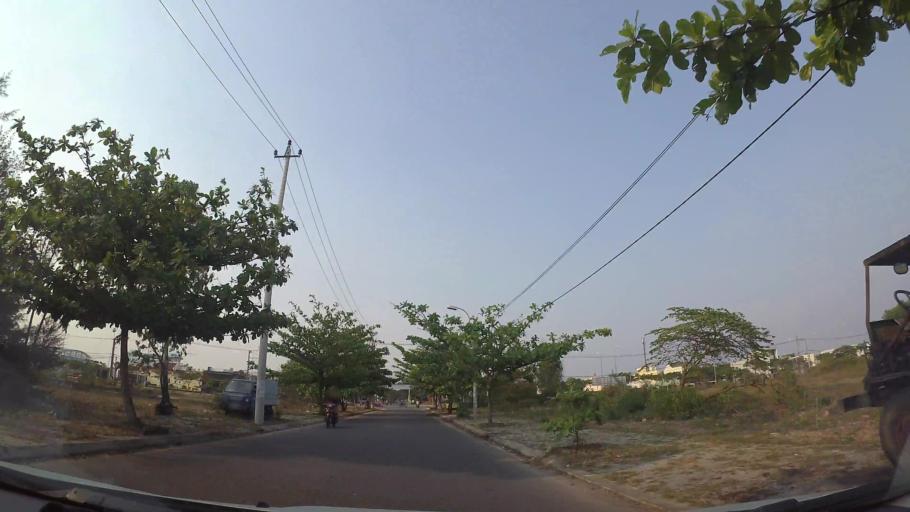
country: VN
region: Da Nang
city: Ngu Hanh Son
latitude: 15.9771
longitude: 108.2501
